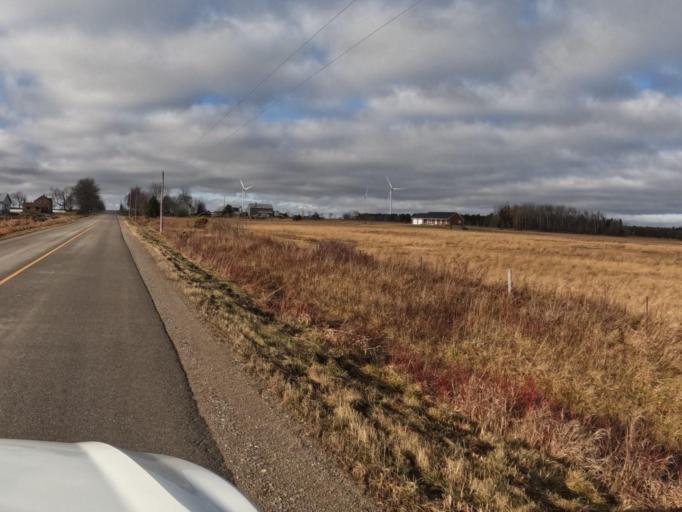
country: CA
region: Ontario
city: Shelburne
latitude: 43.8920
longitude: -80.3490
